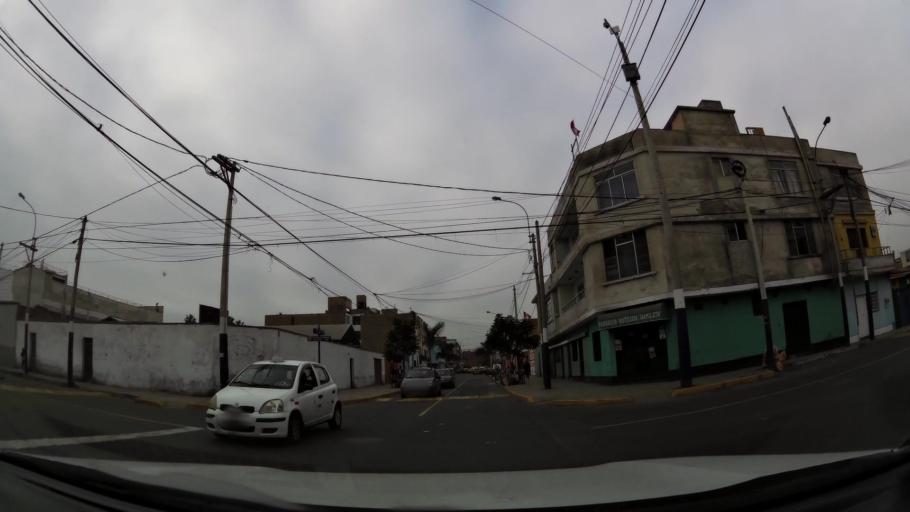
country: PE
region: Lima
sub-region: Lima
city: Surco
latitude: -12.1694
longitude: -77.0255
